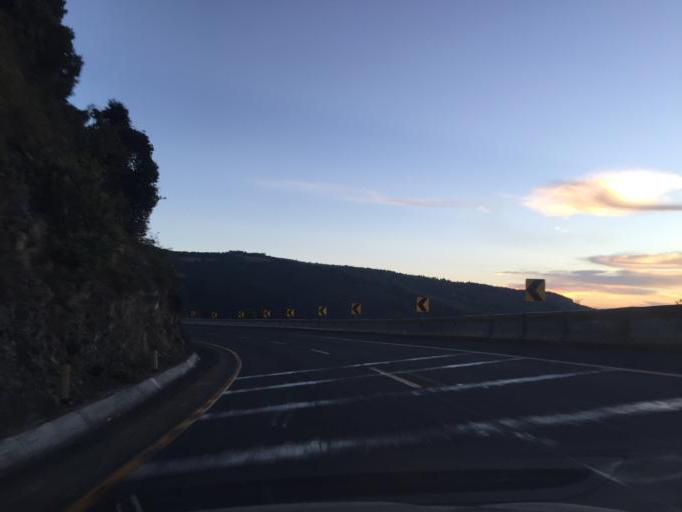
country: MX
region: Puebla
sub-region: Esperanza
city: San Jose Cuyachapa
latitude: 18.8249
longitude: -97.3059
